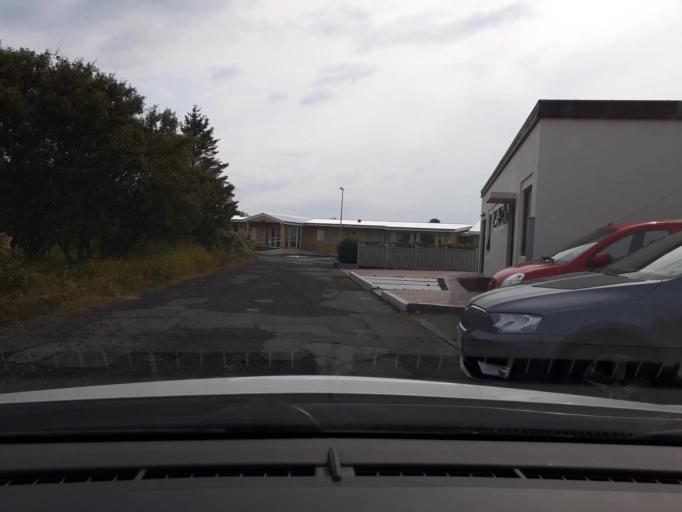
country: IS
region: Southern Peninsula
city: Reykjanesbaer
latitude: 63.9886
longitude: -22.5543
